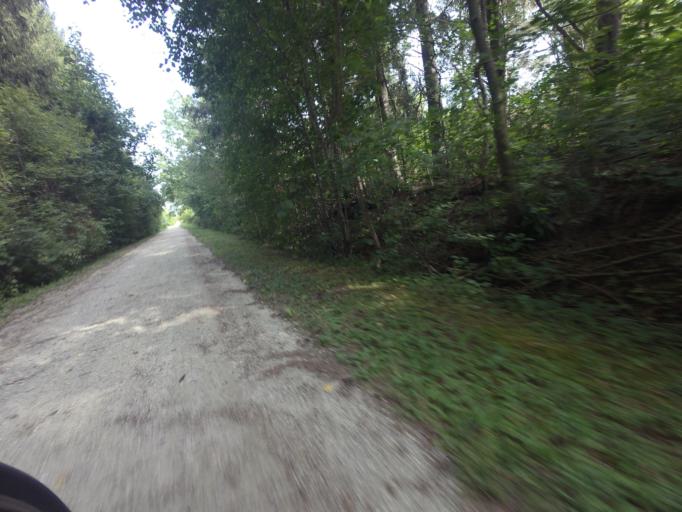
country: CA
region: Ontario
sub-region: Wellington County
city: Guelph
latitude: 43.5767
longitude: -80.3740
